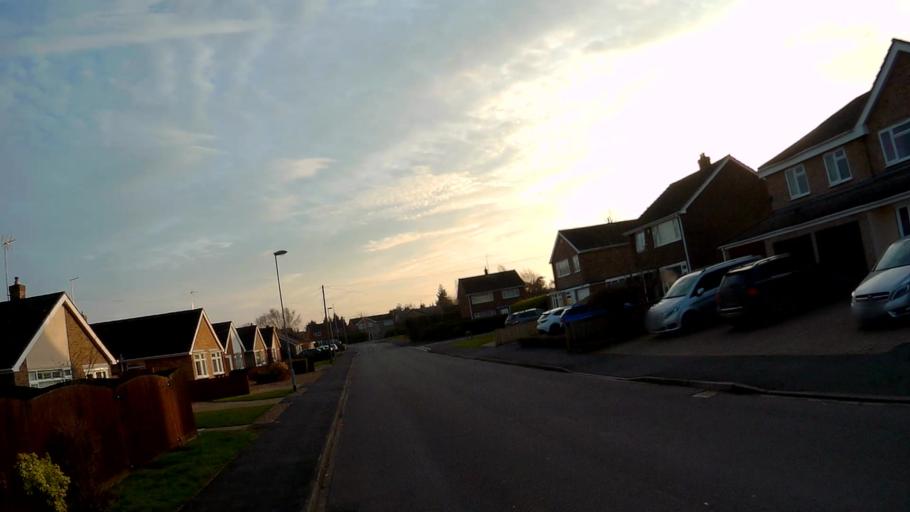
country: GB
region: England
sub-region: Lincolnshire
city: Bourne
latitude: 52.7677
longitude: -0.3926
